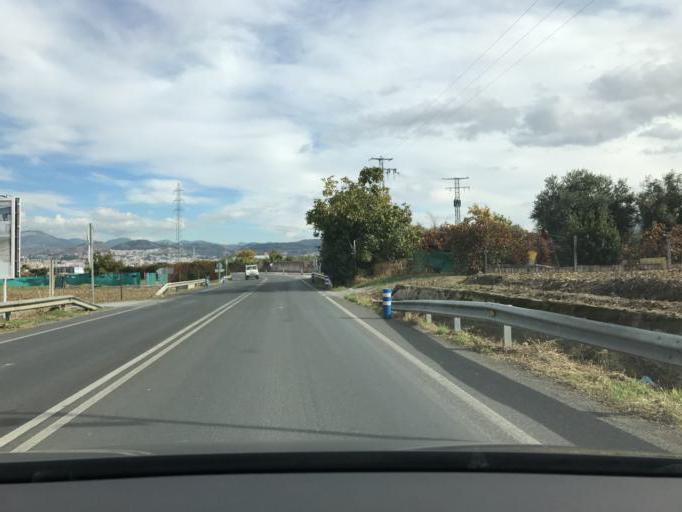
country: ES
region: Andalusia
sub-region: Provincia de Granada
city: Churriana de la Vega
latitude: 37.1539
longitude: -3.6461
